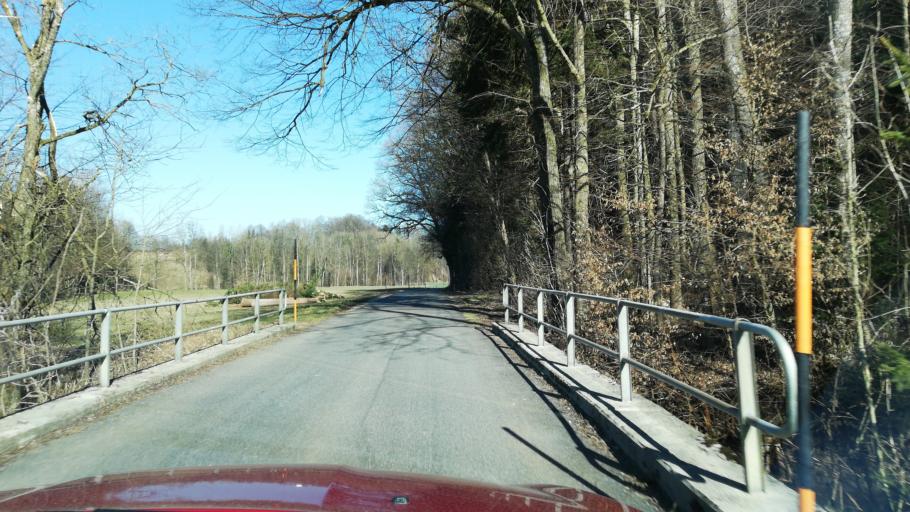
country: AT
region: Upper Austria
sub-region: Politischer Bezirk Vocklabruck
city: Aurach am Hongar
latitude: 47.9625
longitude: 13.6960
